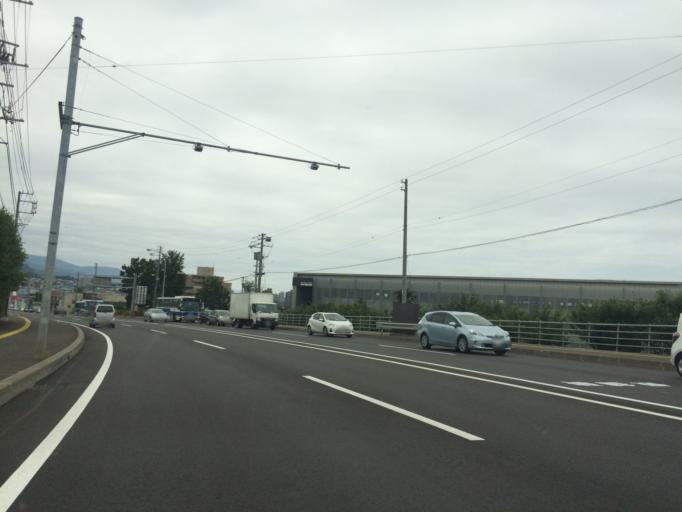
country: JP
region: Hokkaido
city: Sapporo
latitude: 43.1212
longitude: 141.2354
